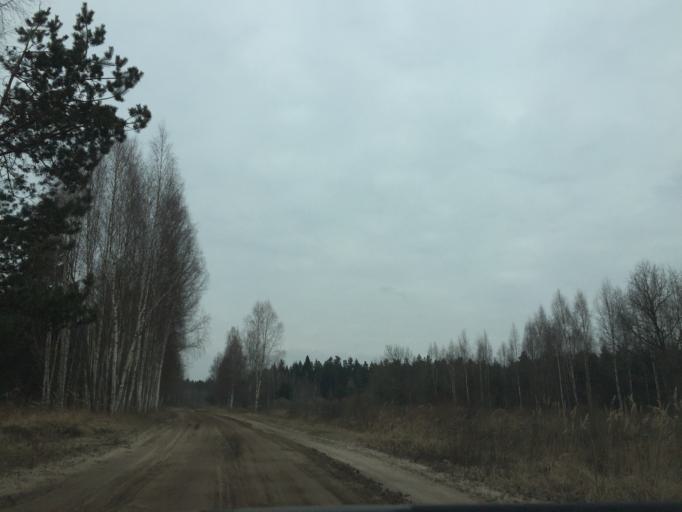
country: LV
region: Kekava
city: Balozi
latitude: 56.7789
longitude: 24.1261
